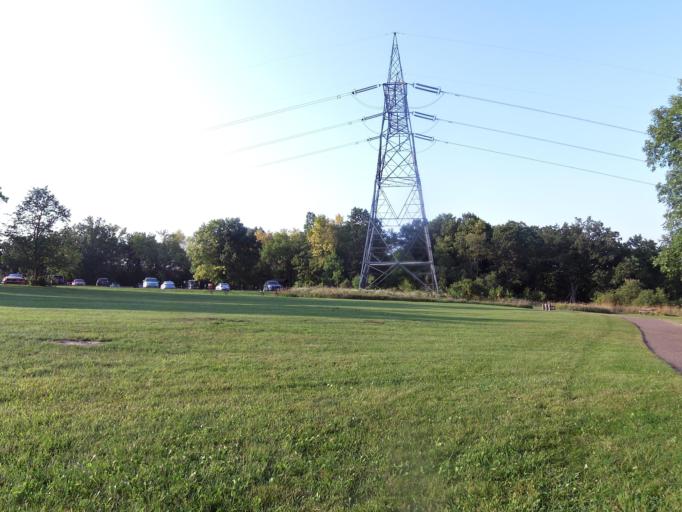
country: US
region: Minnesota
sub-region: Washington County
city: Afton
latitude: 44.8546
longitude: -92.7743
